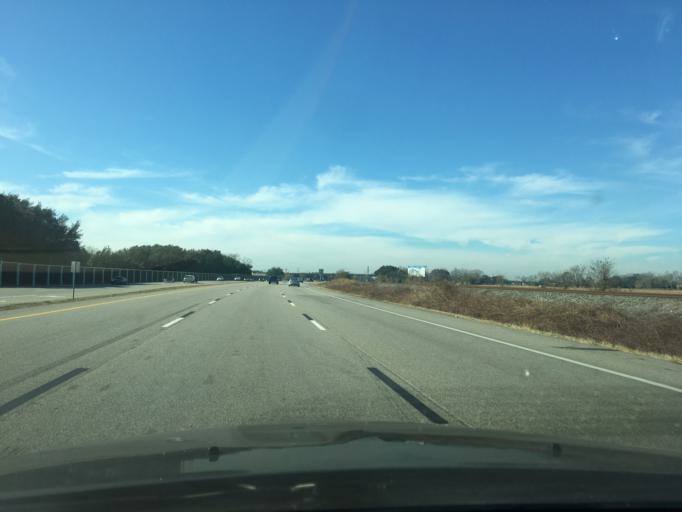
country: US
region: Texas
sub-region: Fort Bend County
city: New Territory
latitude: 29.6033
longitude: -95.6746
